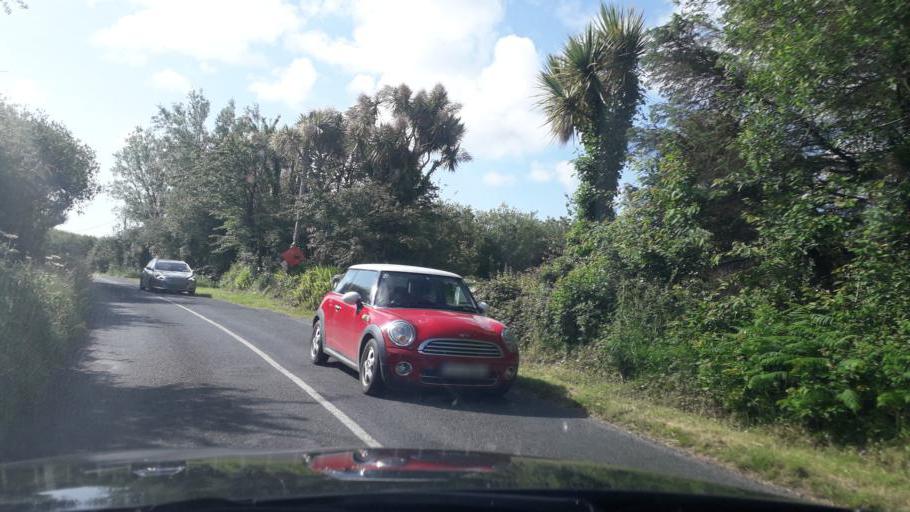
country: IE
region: Leinster
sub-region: Loch Garman
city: Loch Garman
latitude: 52.2583
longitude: -6.5545
